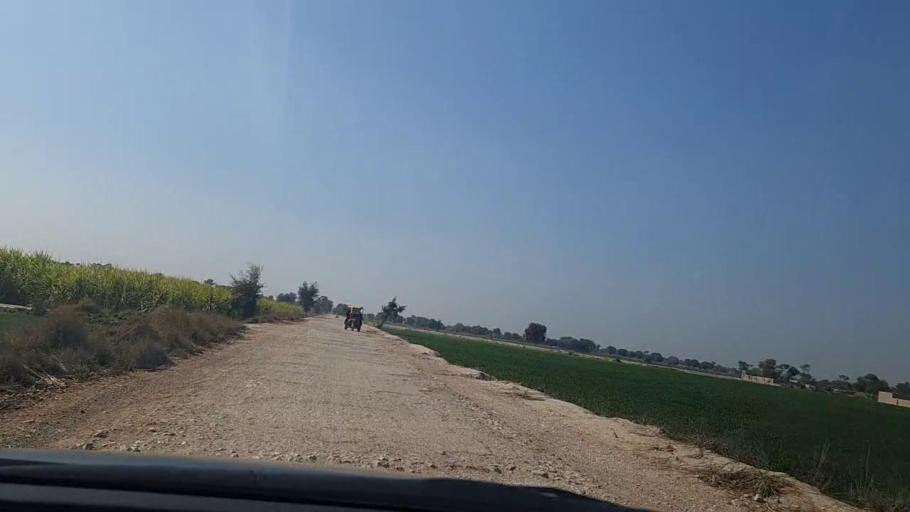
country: PK
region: Sindh
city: Daulatpur
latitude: 26.2846
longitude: 68.0561
